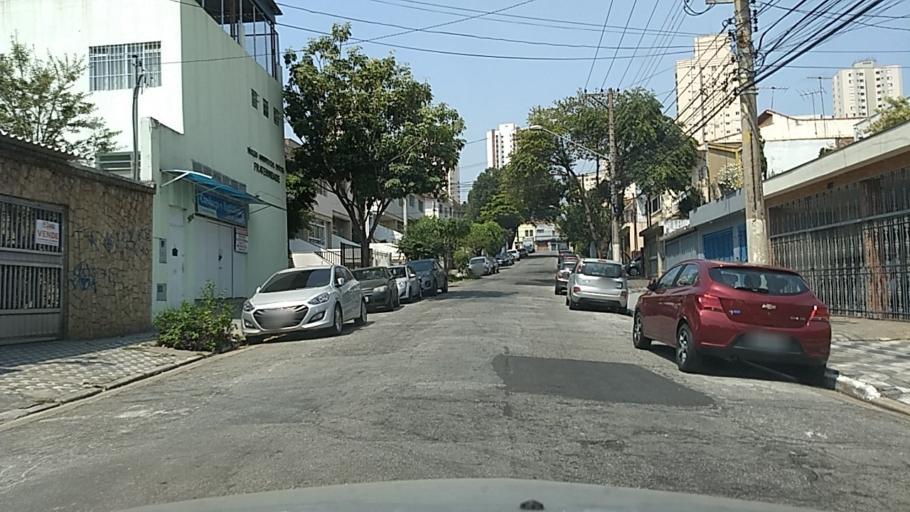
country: BR
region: Sao Paulo
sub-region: Sao Paulo
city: Sao Paulo
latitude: -23.5334
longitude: -46.5774
